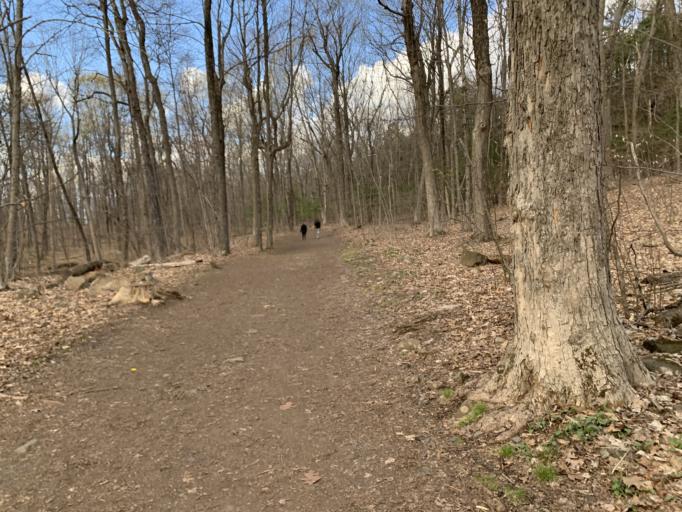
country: US
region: Connecticut
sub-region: Hartford County
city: Weatogue
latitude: 41.8326
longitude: -72.7979
